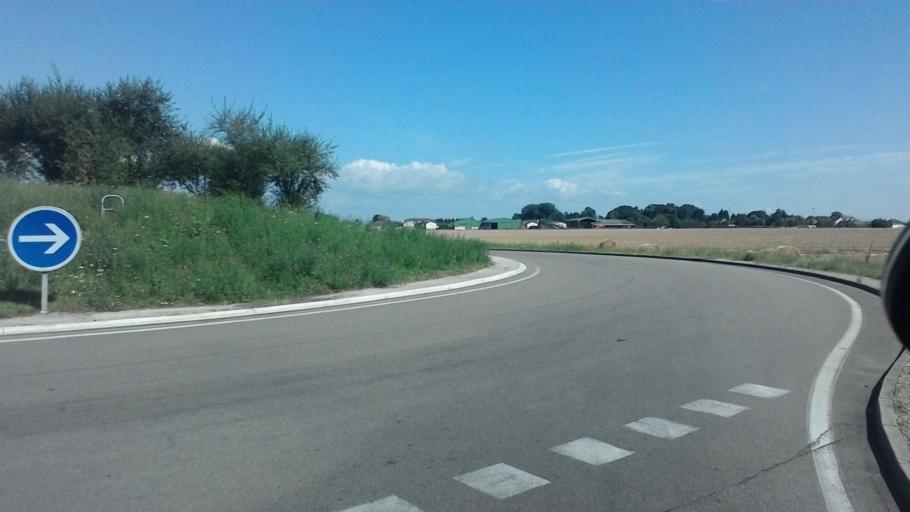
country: FR
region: Bourgogne
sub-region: Departement de Saone-et-Loire
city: Sevrey
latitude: 46.7429
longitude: 4.8530
